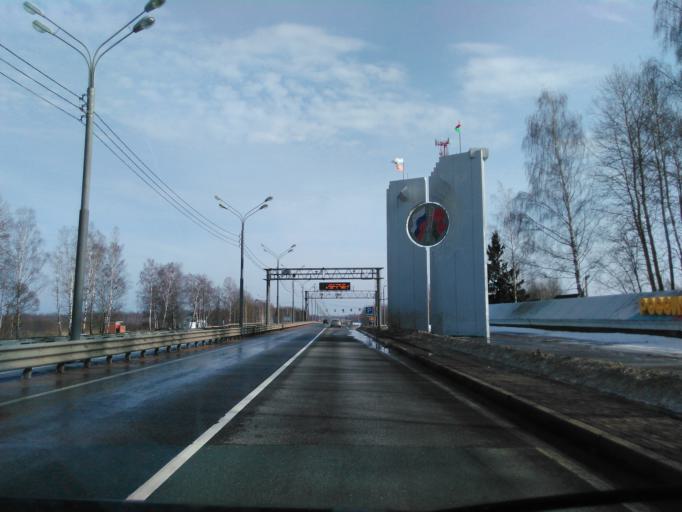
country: RU
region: Smolensk
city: Rudnya
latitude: 54.6907
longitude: 30.9879
